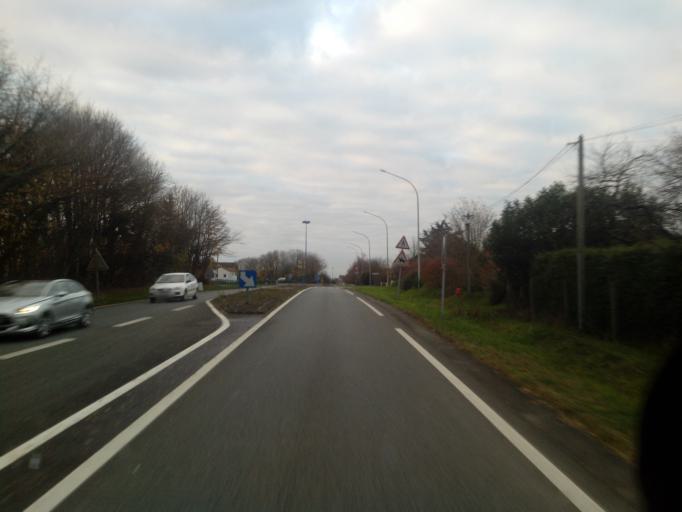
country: FR
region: Poitou-Charentes
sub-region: Departement de la Vienne
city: Mignaloux-Beauvoir
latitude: 46.5659
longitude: 0.3963
